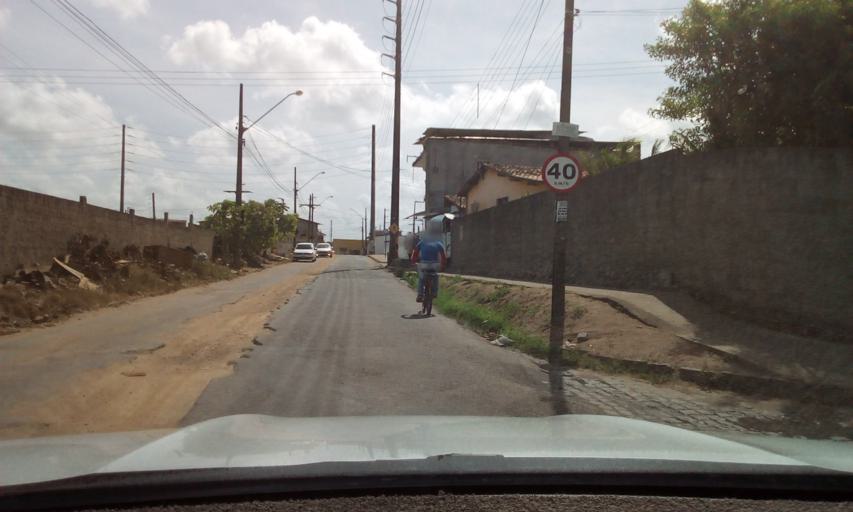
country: BR
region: Paraiba
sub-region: Joao Pessoa
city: Joao Pessoa
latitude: -7.1743
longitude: -34.8884
